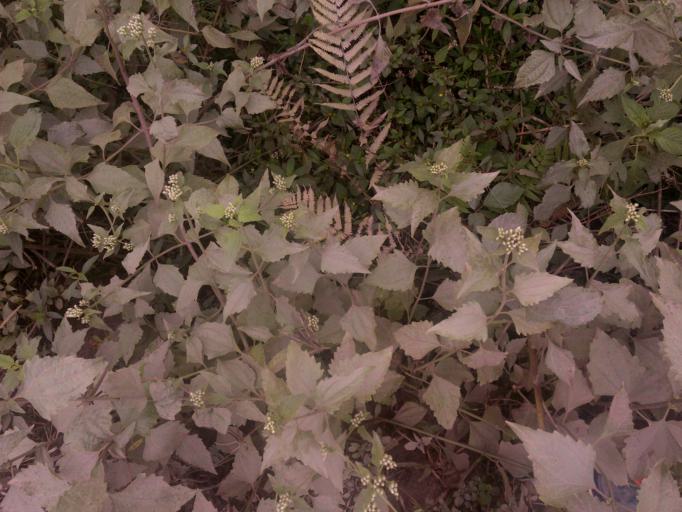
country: LA
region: Xiangkhoang
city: Muang Phonsavan
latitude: 19.3331
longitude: 103.6432
